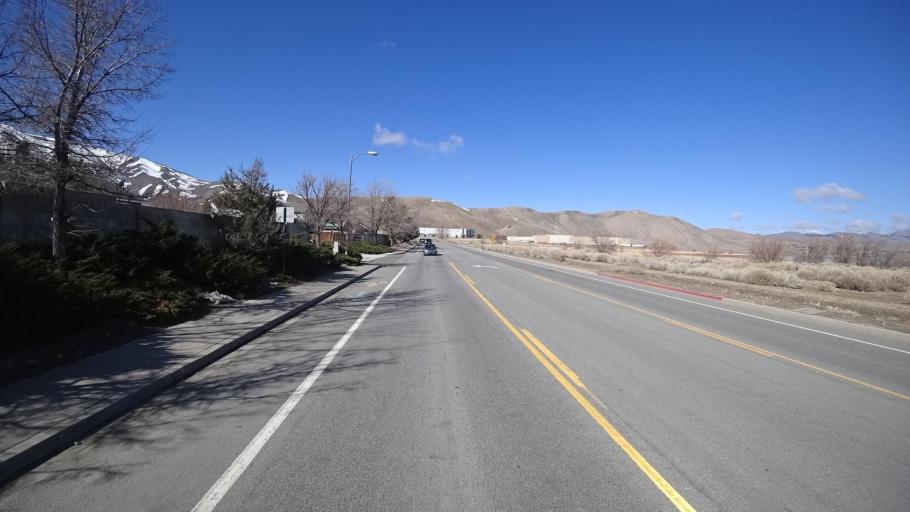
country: US
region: Nevada
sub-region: Washoe County
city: Lemmon Valley
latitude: 39.6347
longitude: -119.9059
